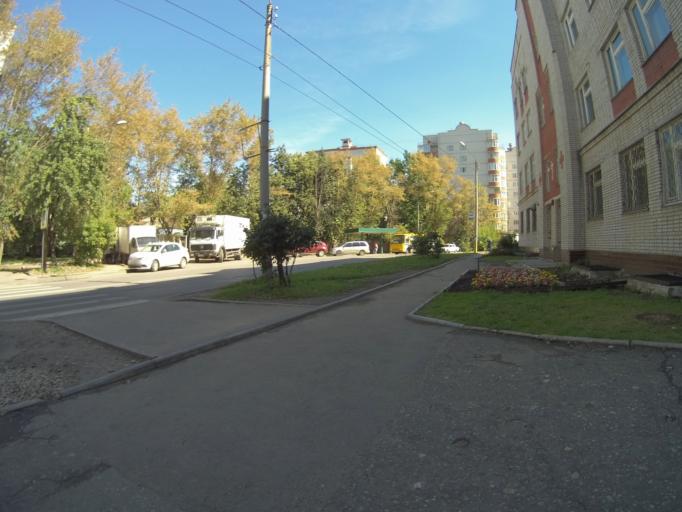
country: RU
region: Vladimir
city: Vladimir
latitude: 56.1302
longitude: 40.3696
